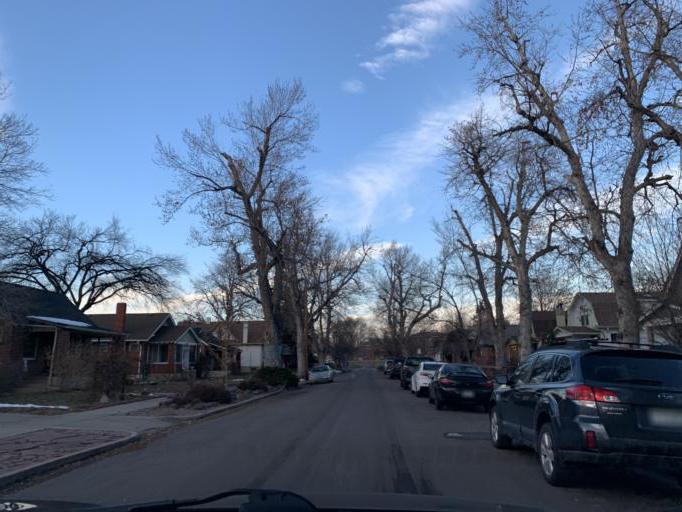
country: US
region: Colorado
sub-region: Jefferson County
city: Edgewater
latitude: 39.7716
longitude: -105.0358
